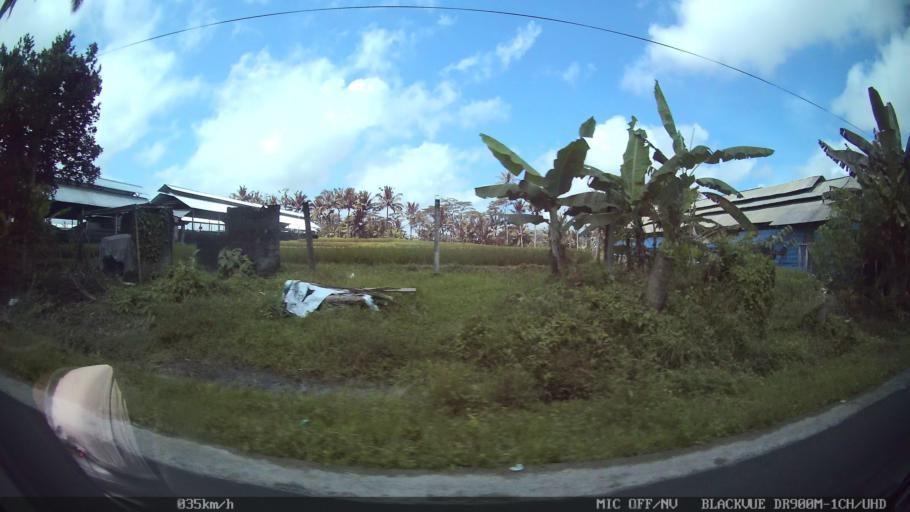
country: ID
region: Bali
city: Banjar Apuan Kaja
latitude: -8.4854
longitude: 115.3428
